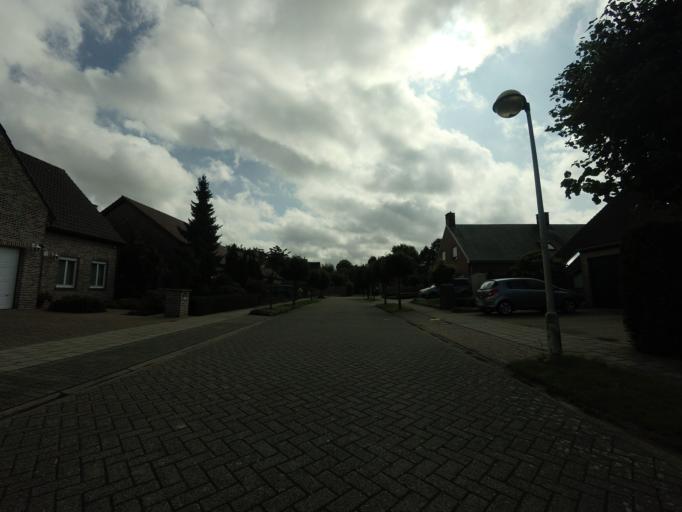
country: BE
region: Flanders
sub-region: Provincie Antwerpen
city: Rumst
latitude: 51.1039
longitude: 4.4164
